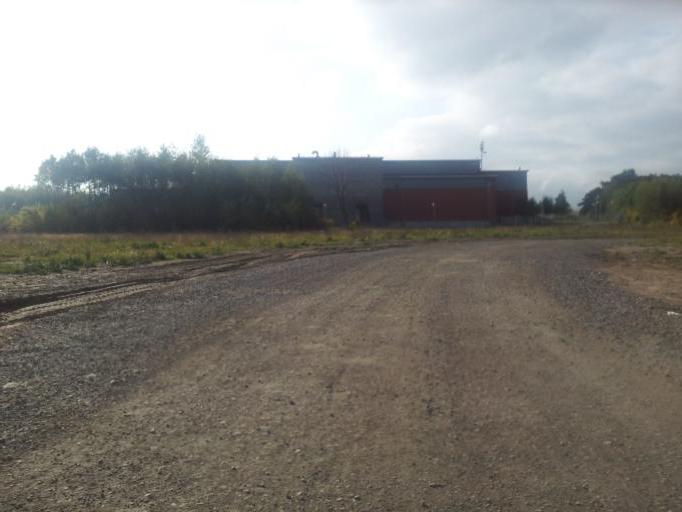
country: SE
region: Uppsala
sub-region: Uppsala Kommun
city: Gamla Uppsala
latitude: 59.8844
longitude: 17.6672
